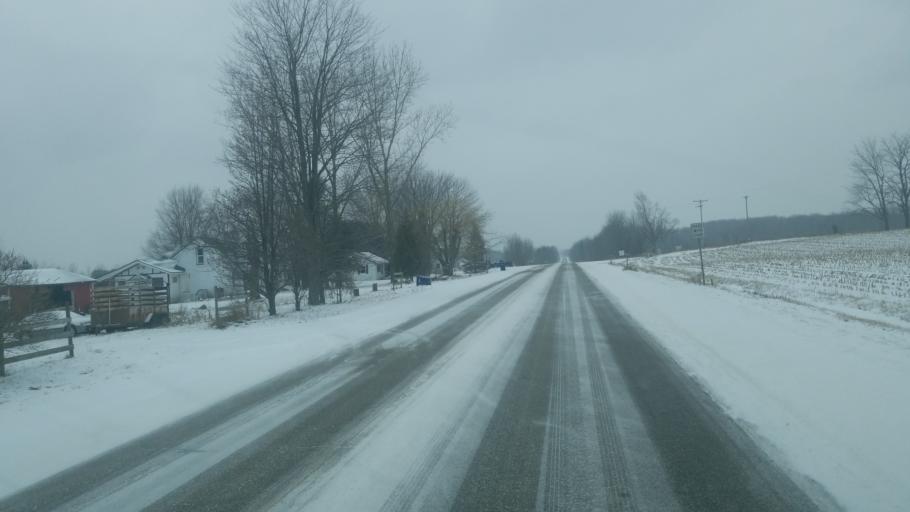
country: US
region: Michigan
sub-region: Osceola County
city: Evart
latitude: 44.1025
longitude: -85.1857
